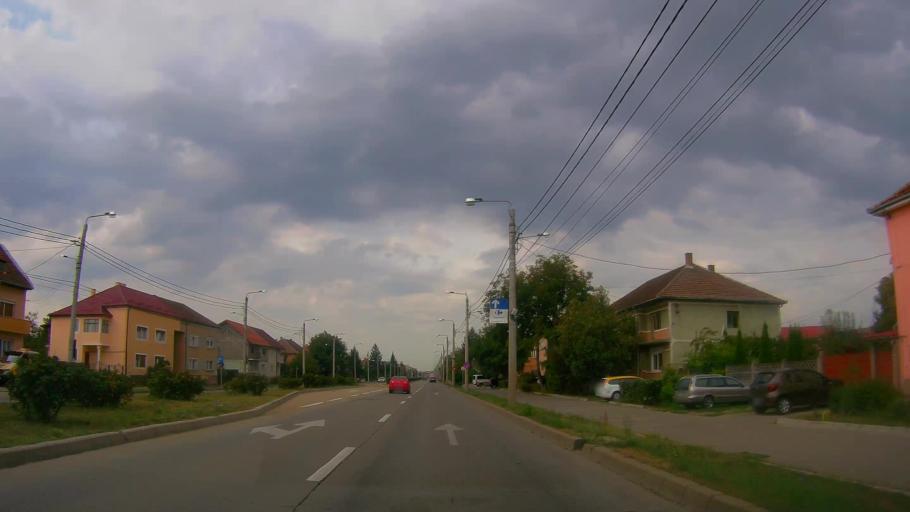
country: RO
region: Satu Mare
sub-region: Comuna Paulesti
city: Paulesti
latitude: 47.8052
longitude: 22.9114
